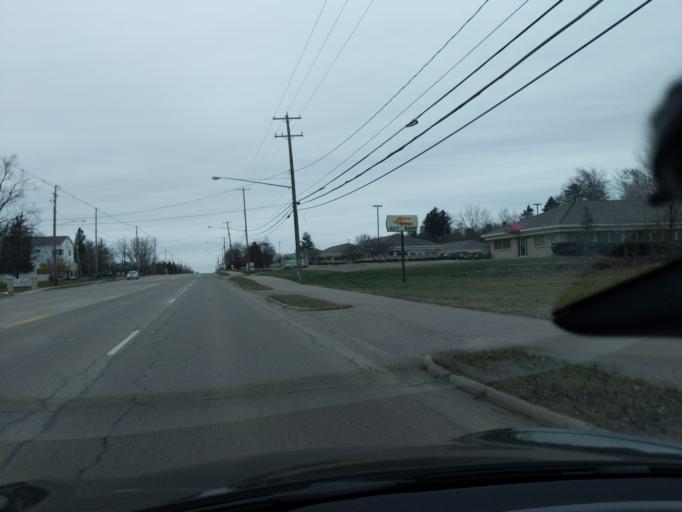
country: US
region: Michigan
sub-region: Ingham County
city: Lansing
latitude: 42.7856
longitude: -84.5426
